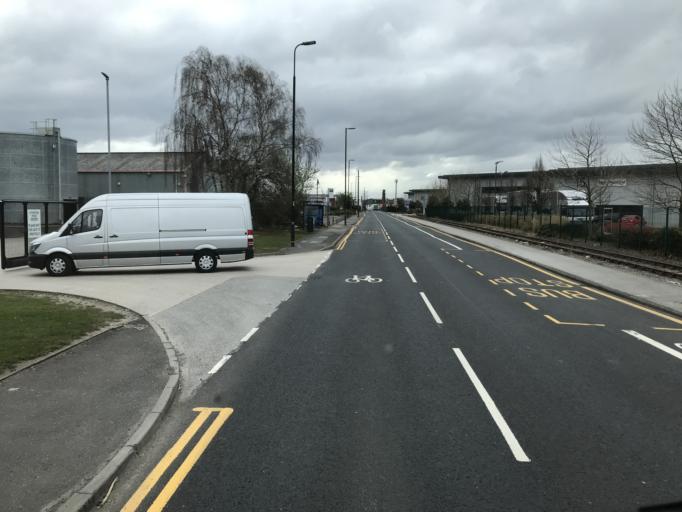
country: GB
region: England
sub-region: Trafford
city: Trafford Park
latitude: 53.4713
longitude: -2.3144
